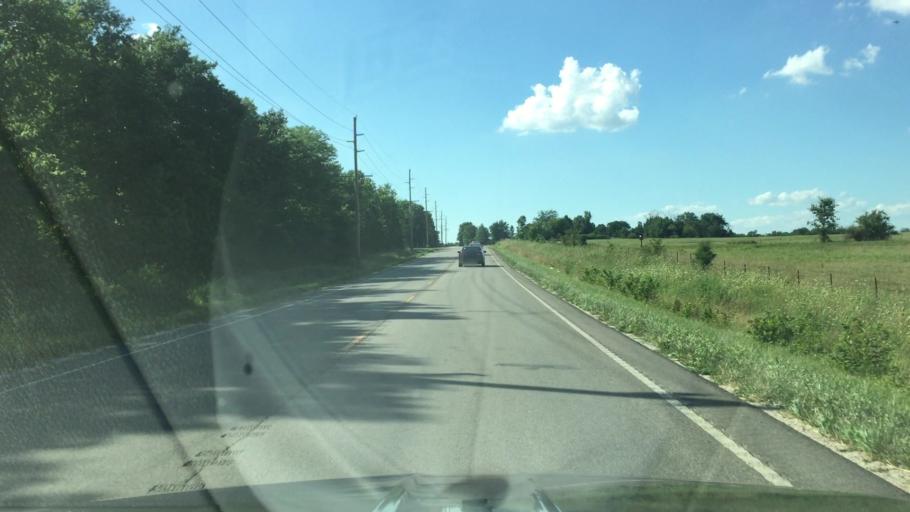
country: US
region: Missouri
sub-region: Morgan County
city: Versailles
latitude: 38.4378
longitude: -92.7847
